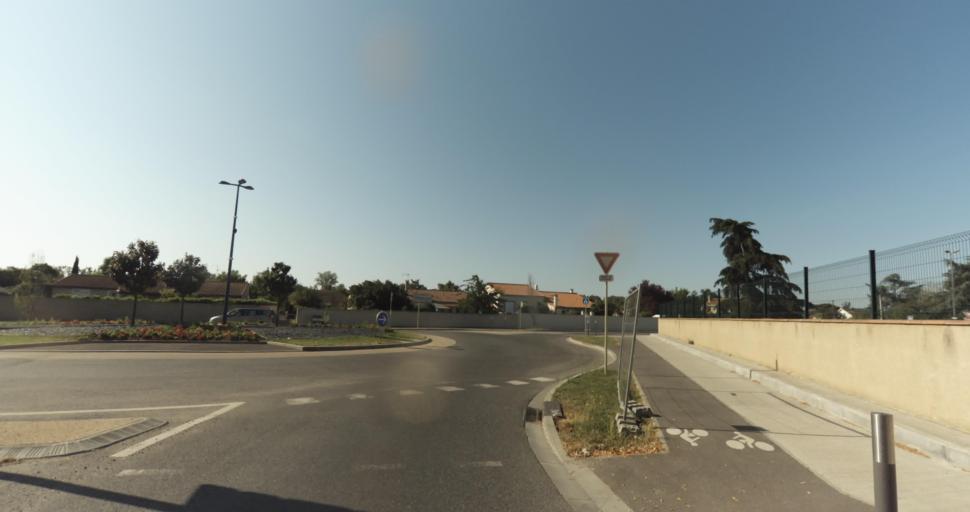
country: FR
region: Midi-Pyrenees
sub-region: Departement de la Haute-Garonne
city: Plaisance-du-Touch
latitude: 43.5617
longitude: 1.2926
